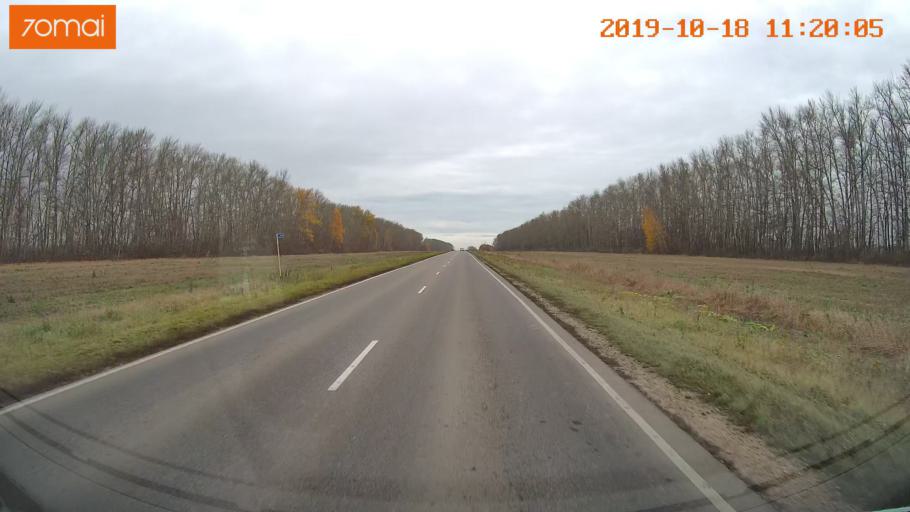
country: RU
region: Tula
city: Kimovsk
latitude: 54.0550
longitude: 38.5569
